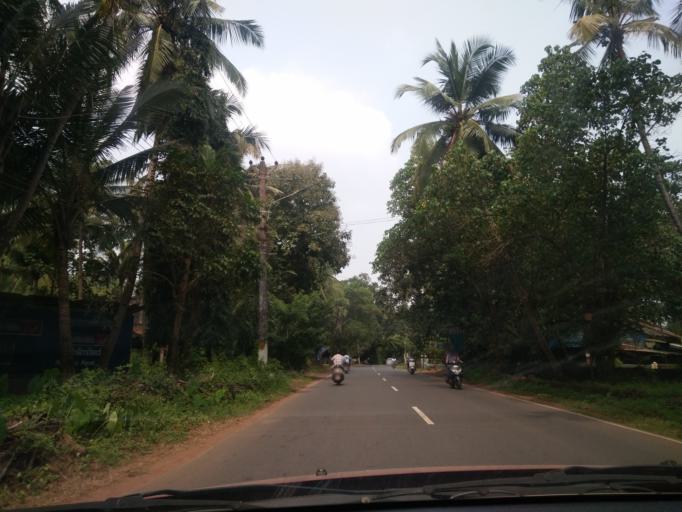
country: IN
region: Goa
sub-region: North Goa
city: Goa Velha
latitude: 15.4369
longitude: 73.8925
